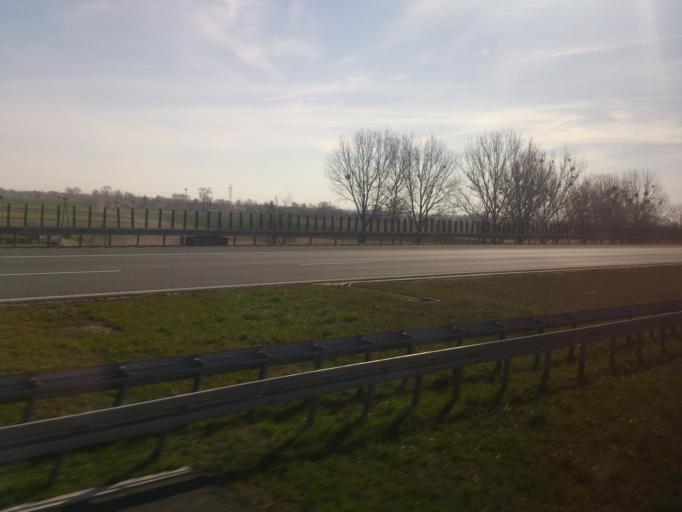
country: PL
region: Kujawsko-Pomorskie
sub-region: Powiat aleksandrowski
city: Waganiec
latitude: 52.7942
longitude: 18.8365
